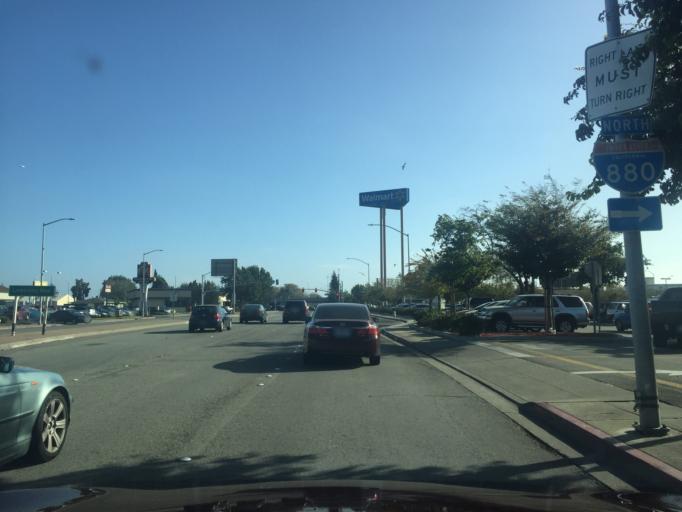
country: US
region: California
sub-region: Alameda County
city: San Lorenzo
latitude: 37.6882
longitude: -122.1302
